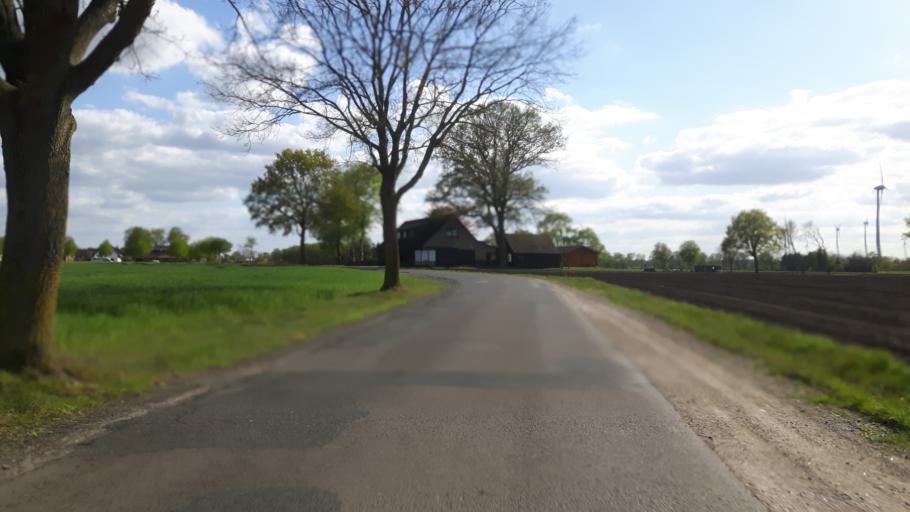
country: DE
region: Lower Saxony
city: Kirchseelte
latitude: 52.9989
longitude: 8.6892
